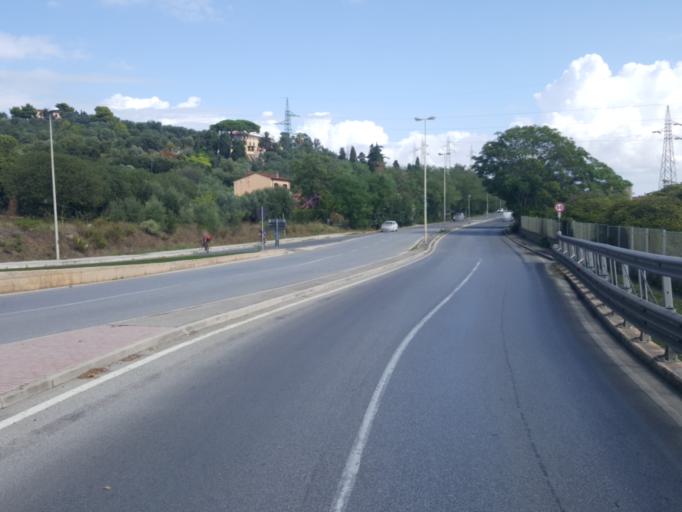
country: IT
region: Tuscany
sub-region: Provincia di Livorno
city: Piombino
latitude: 42.9371
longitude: 10.5300
